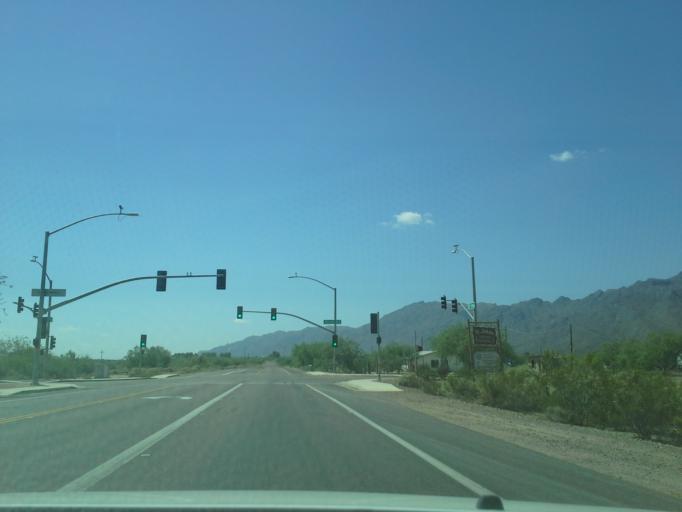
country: US
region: Arizona
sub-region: Maricopa County
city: Laveen
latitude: 33.2910
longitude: -112.1691
